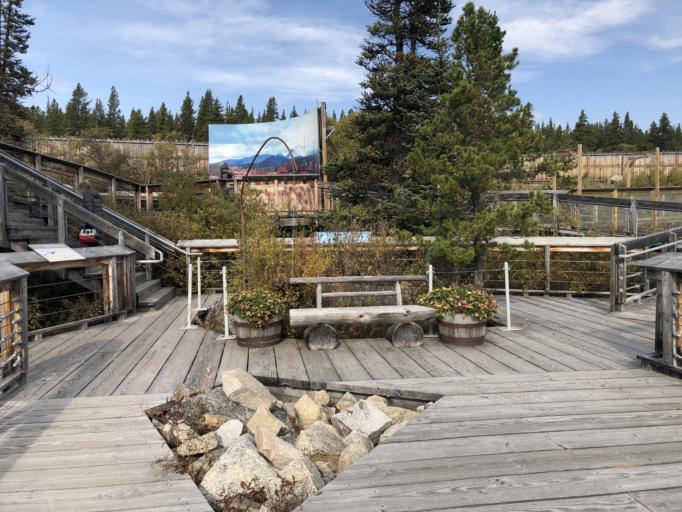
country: US
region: Alaska
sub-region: Haines Borough
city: Haines
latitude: 59.7752
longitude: -134.9166
